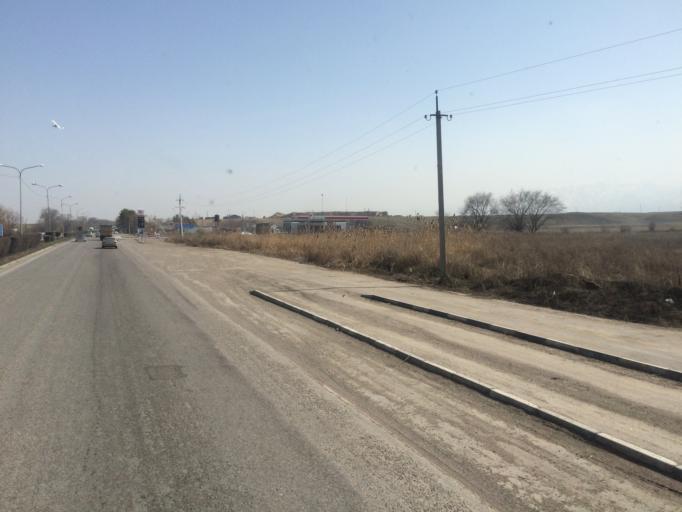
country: KZ
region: Almaty Oblysy
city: Burunday
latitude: 43.2224
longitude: 76.4223
